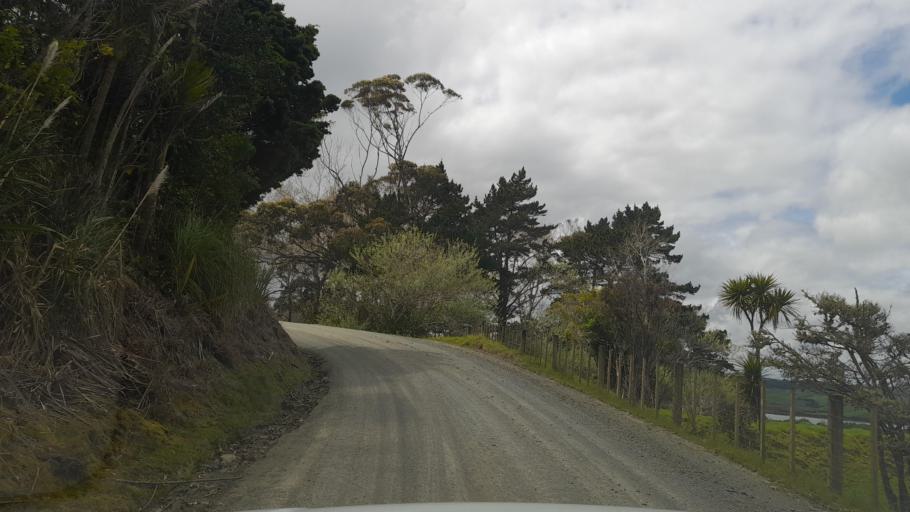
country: NZ
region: Auckland
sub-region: Auckland
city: Wellsford
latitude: -36.1785
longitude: 174.3484
